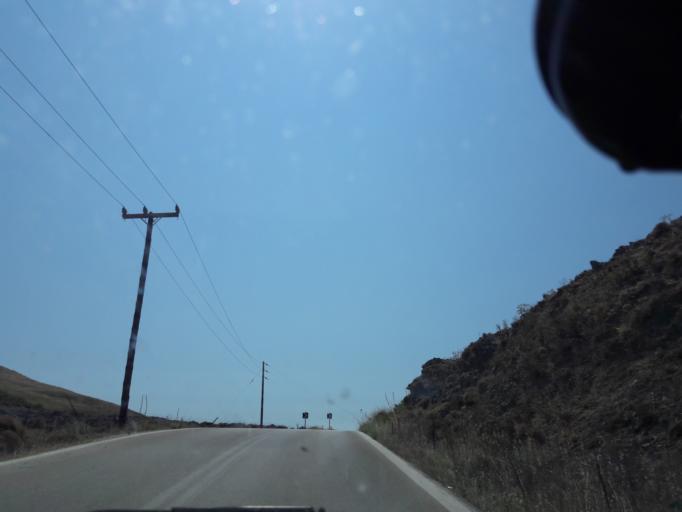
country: GR
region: North Aegean
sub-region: Nomos Lesvou
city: Myrina
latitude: 39.8509
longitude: 25.0942
